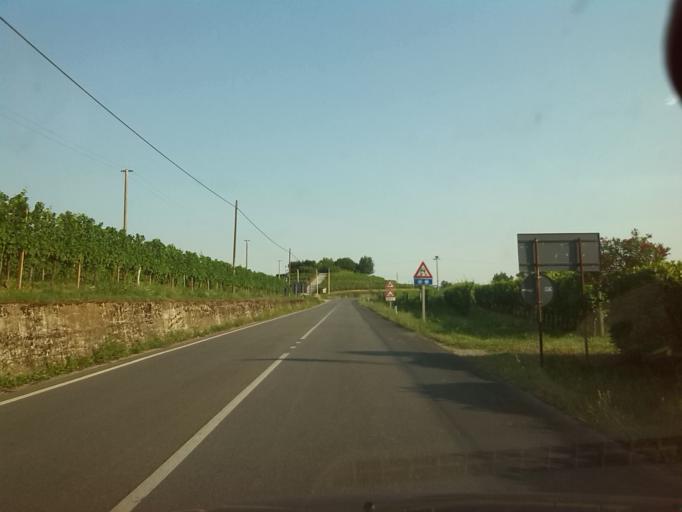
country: IT
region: Friuli Venezia Giulia
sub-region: Provincia di Udine
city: Prepotto
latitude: 46.0417
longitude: 13.4774
